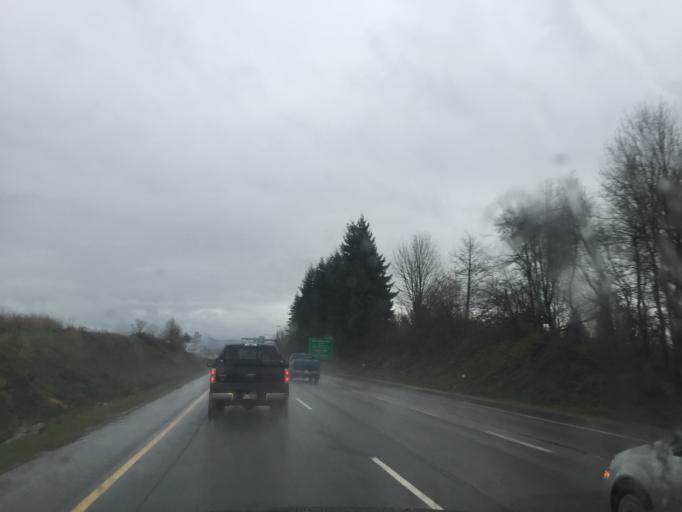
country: CA
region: British Columbia
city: Aldergrove
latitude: 49.0614
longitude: -122.3913
